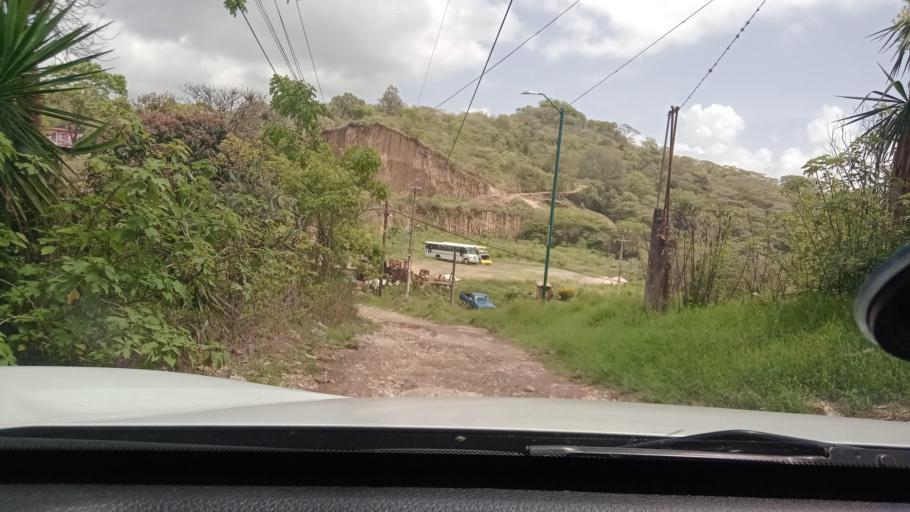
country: MX
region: Veracruz
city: El Castillo
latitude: 19.5495
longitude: -96.8620
